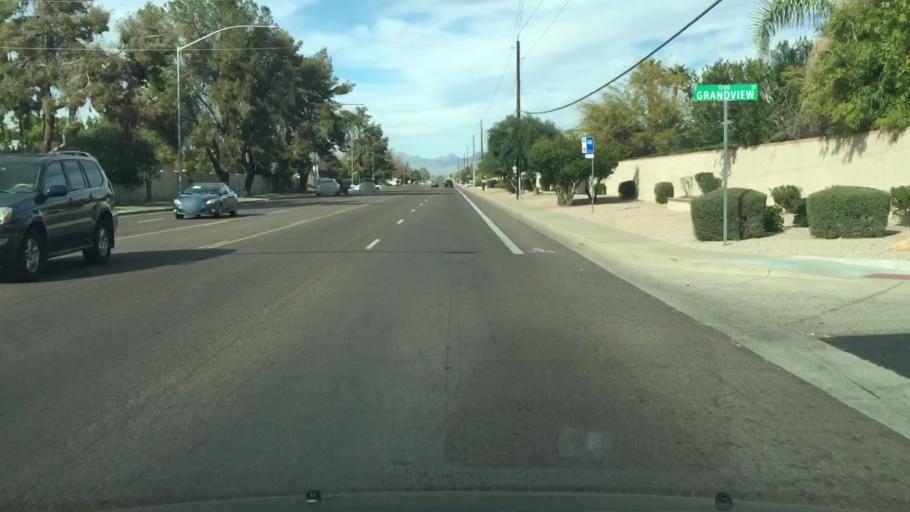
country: US
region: Arizona
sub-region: Maricopa County
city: Mesa
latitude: 33.4399
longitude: -111.8051
